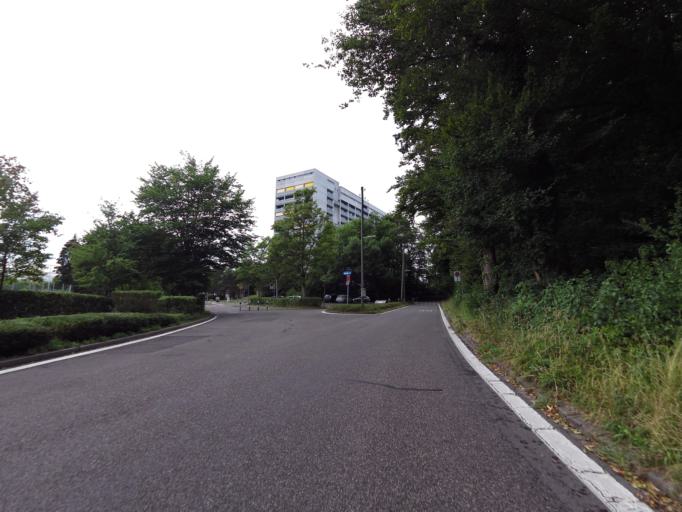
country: CH
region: Zurich
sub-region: Bezirk Zuerich
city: Zuerich (Kreis 11) / Affoltern
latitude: 47.4203
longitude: 8.5140
